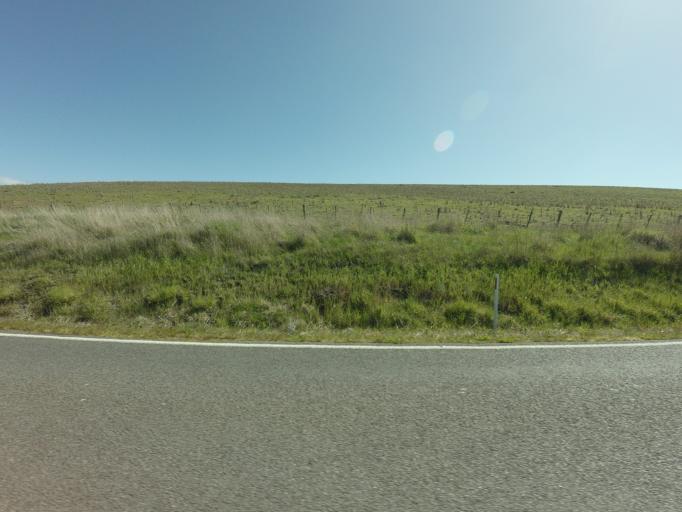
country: AU
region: Tasmania
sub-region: Derwent Valley
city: New Norfolk
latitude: -42.6408
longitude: 146.9190
